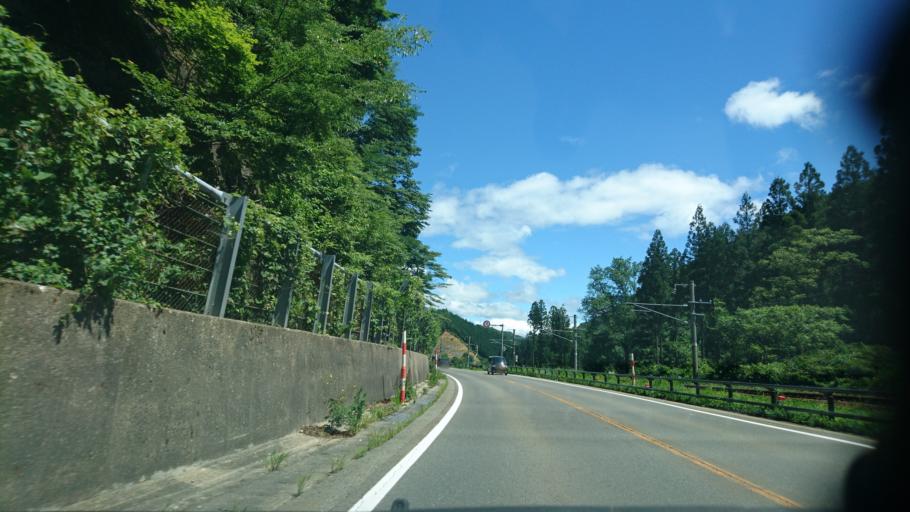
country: JP
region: Akita
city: Kakunodatemachi
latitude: 39.6453
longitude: 140.6641
